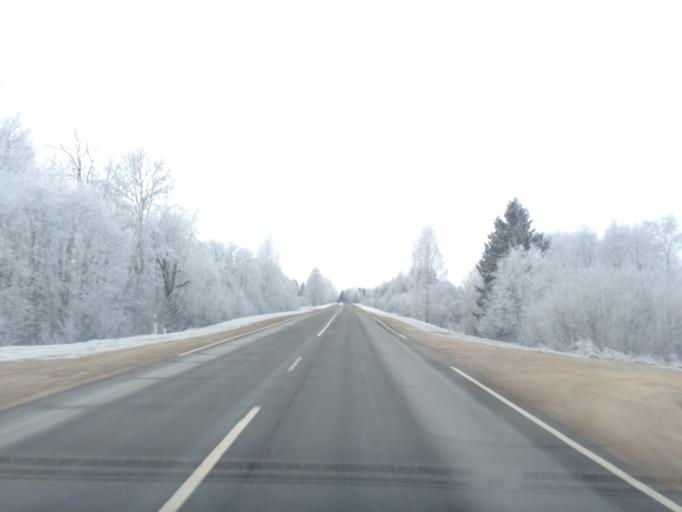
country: LV
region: Rezekne
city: Rezekne
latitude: 56.6343
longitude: 27.4714
